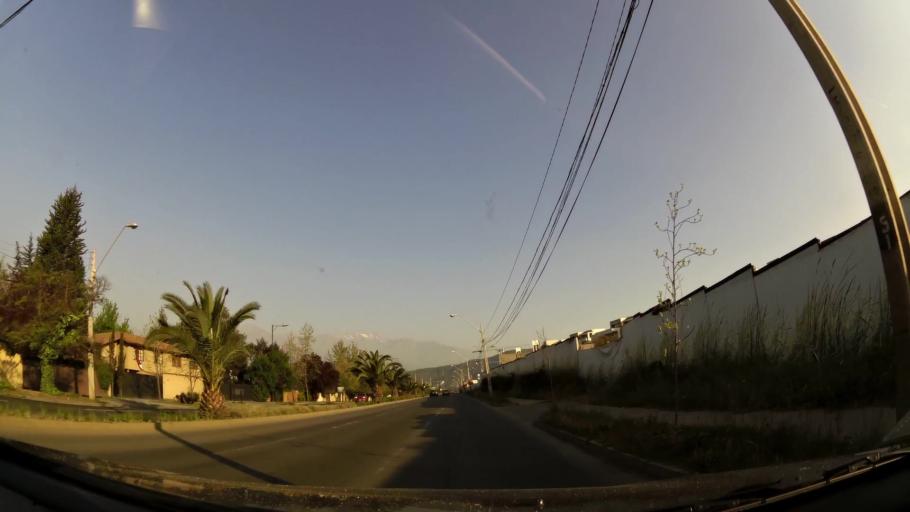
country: CL
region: Santiago Metropolitan
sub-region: Provincia de Santiago
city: Villa Presidente Frei, Nunoa, Santiago, Chile
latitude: -33.3484
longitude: -70.5425
